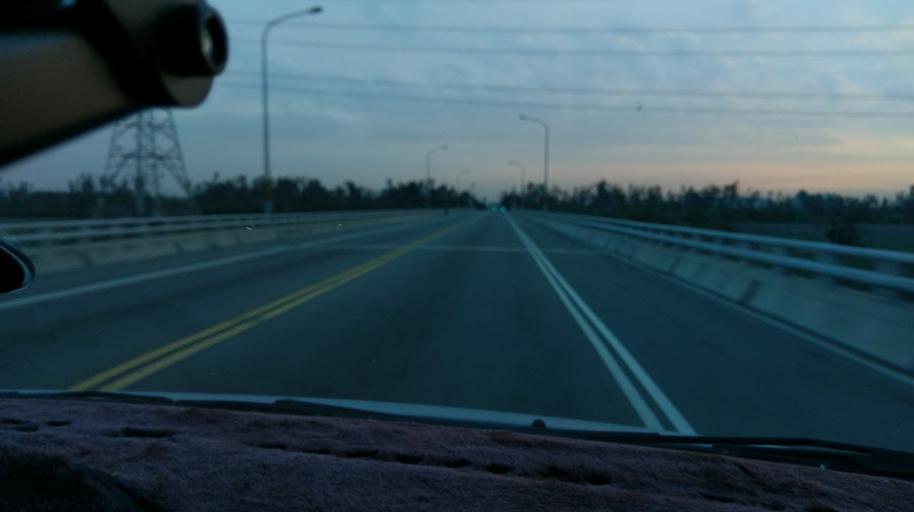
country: TW
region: Taiwan
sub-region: Changhua
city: Chang-hua
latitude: 24.1884
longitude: 120.5064
